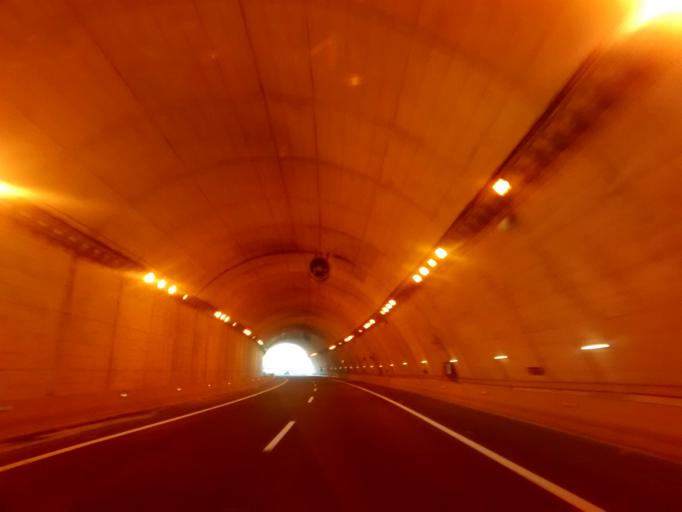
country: ES
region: Cantabria
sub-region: Provincia de Cantabria
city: Comillas
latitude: 43.3337
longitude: -4.3188
